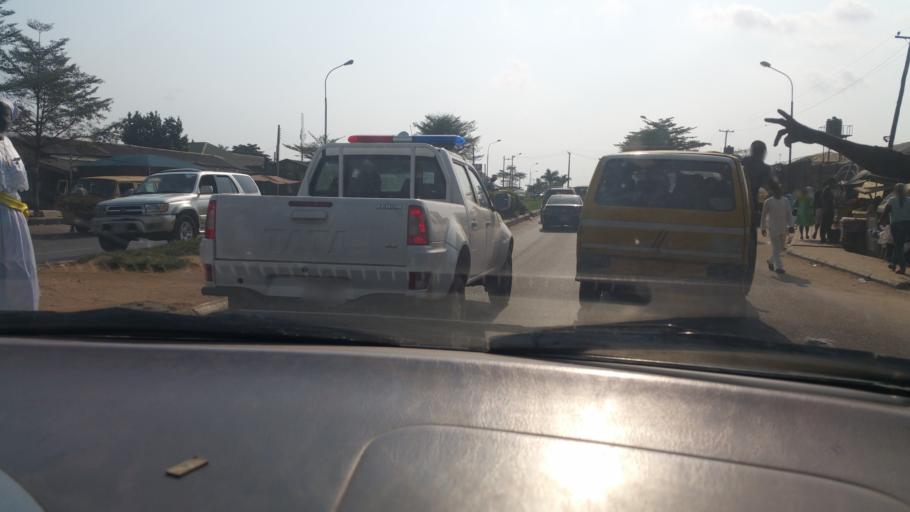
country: NG
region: Lagos
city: Ikotun
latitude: 6.5744
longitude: 3.2567
